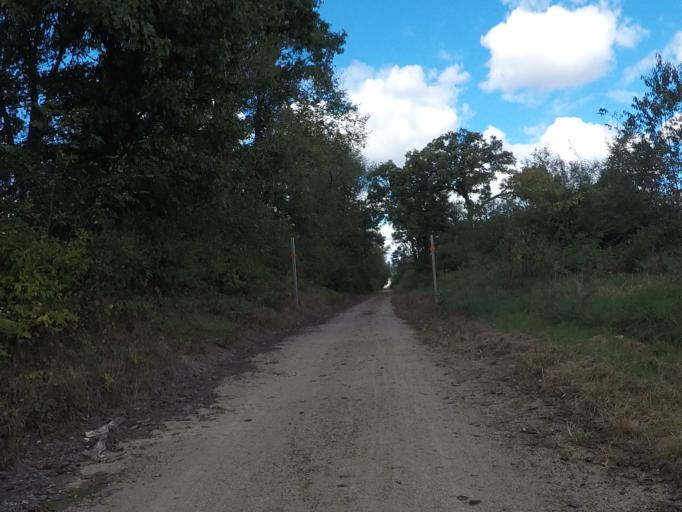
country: US
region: Wisconsin
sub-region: Richland County
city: Richland Center
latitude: 43.3050
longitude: -90.3405
